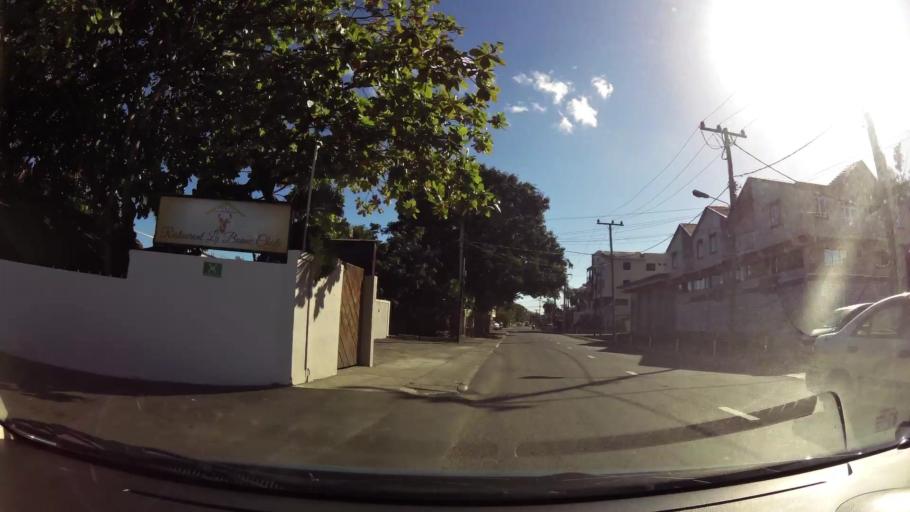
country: MU
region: Black River
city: Grande Riviere Noire
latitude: -20.3455
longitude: 57.3642
